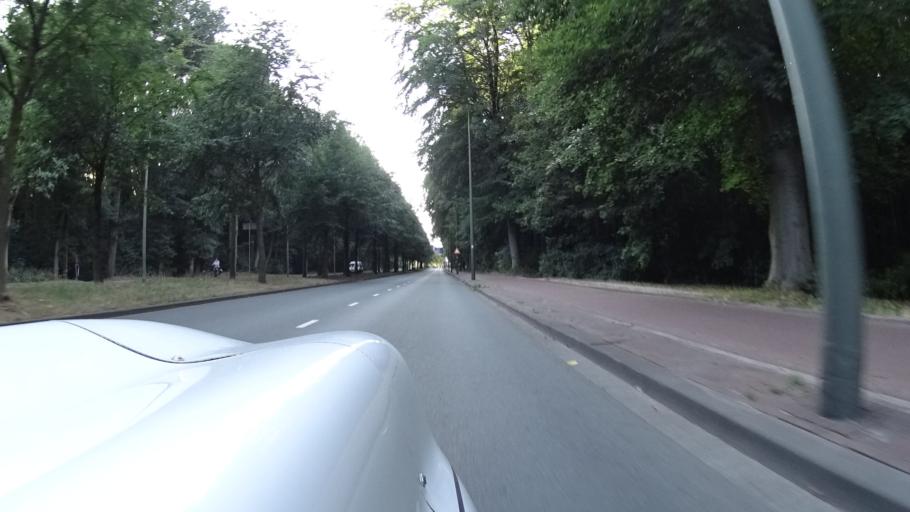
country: NL
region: South Holland
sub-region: Gemeente Leidschendam-Voorburg
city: Voorburg
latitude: 52.0893
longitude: 4.3337
